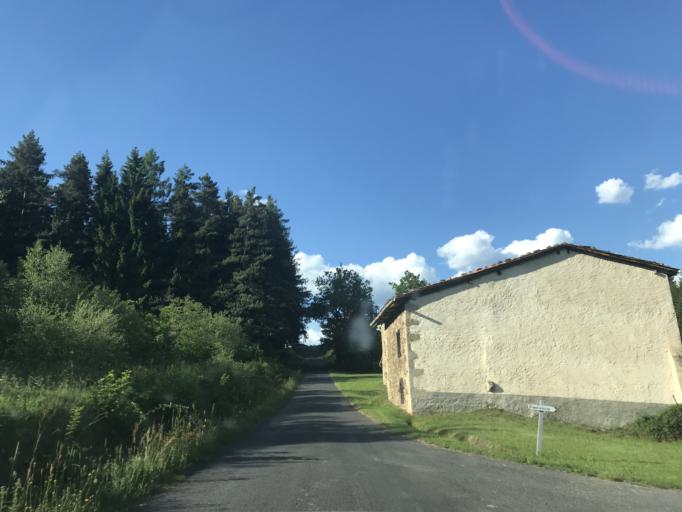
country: FR
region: Auvergne
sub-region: Departement du Puy-de-Dome
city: Job
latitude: 45.6725
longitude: 3.6812
